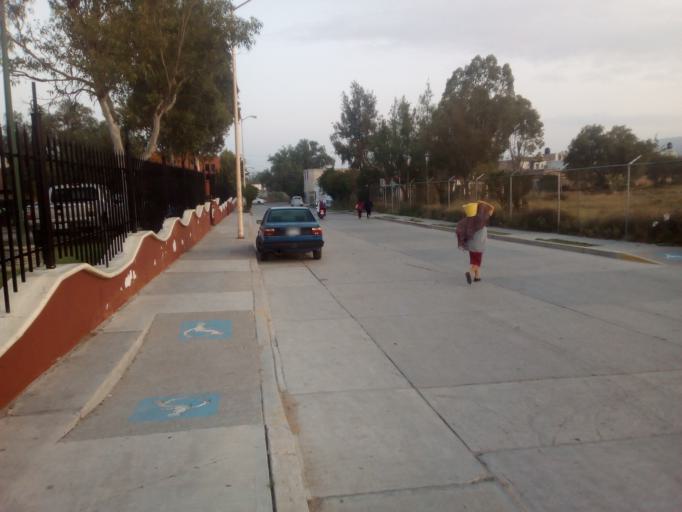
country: MX
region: Guerrero
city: San Luis de la Paz
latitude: 21.2915
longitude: -100.5233
